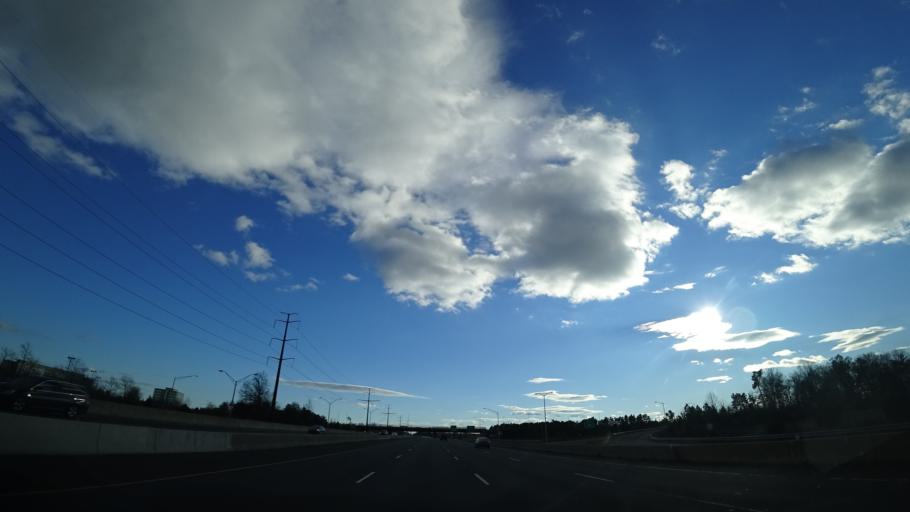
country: US
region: Virginia
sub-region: Fairfax County
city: Chantilly
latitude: 38.9186
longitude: -77.4302
